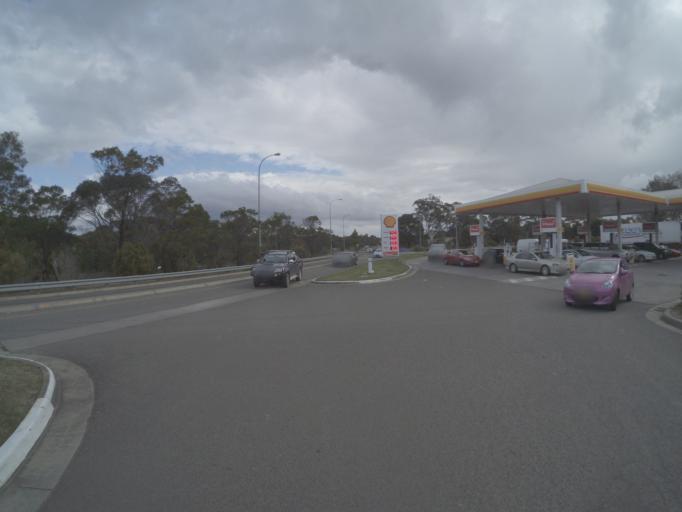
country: AU
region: New South Wales
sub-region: Wingecarribee
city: Bundanoon
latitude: -34.6080
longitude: 150.2254
